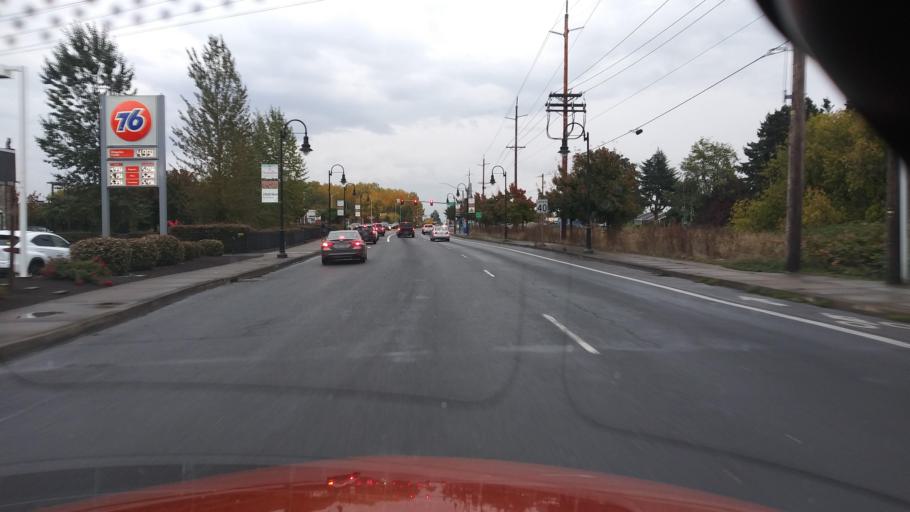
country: US
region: Oregon
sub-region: Washington County
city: Cornelius
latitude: 45.5201
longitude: -123.0489
